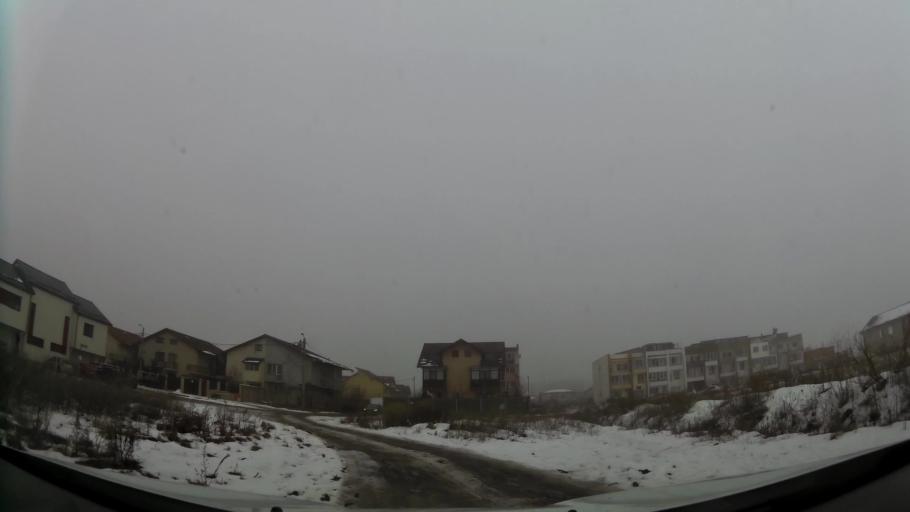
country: RO
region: Ilfov
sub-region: Comuna Chiajna
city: Rosu
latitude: 44.4401
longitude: 25.9933
